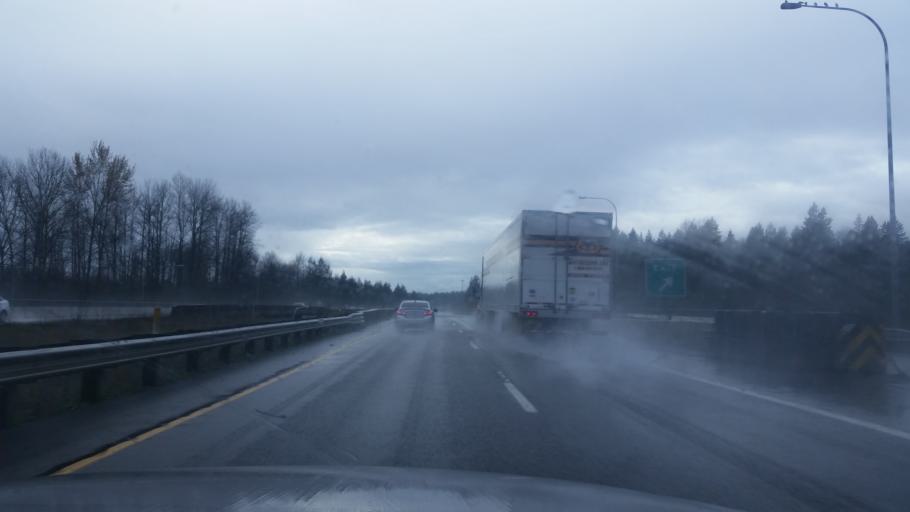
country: US
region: Washington
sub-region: King County
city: Maple Valley
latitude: 47.4163
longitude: -122.0149
